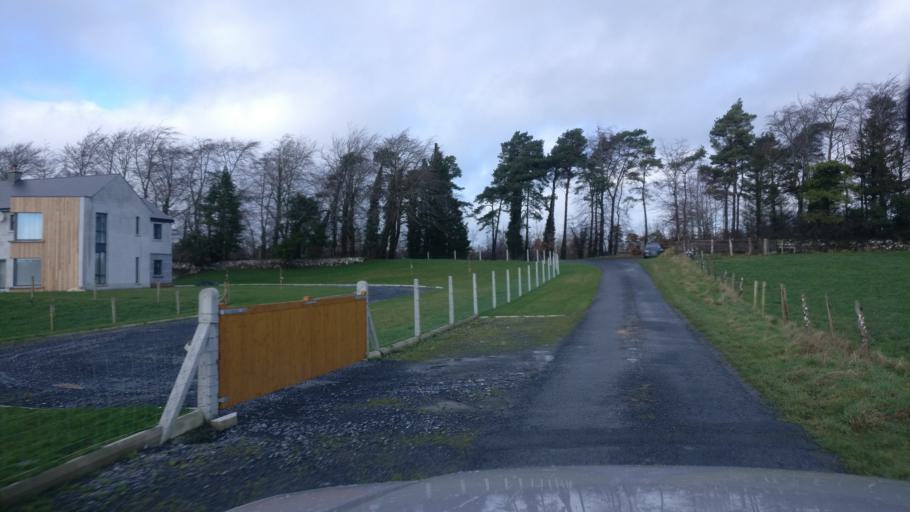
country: IE
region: Connaught
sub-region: County Galway
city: Loughrea
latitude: 53.2423
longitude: -8.6514
